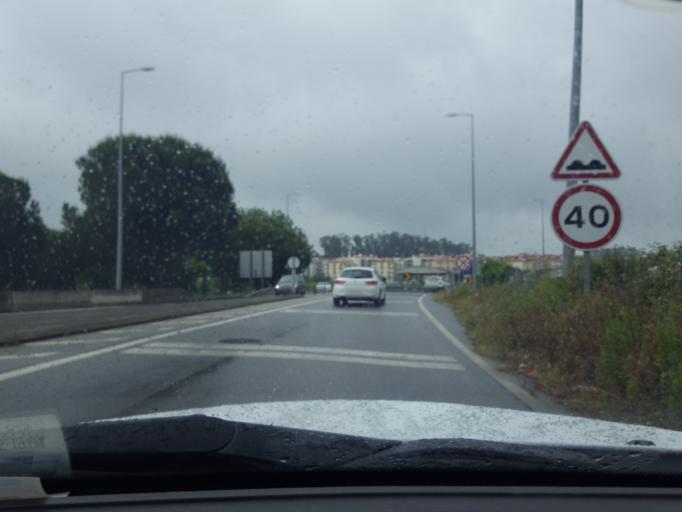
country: PT
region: Leiria
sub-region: Leiria
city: Leiria
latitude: 39.7393
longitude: -8.8182
